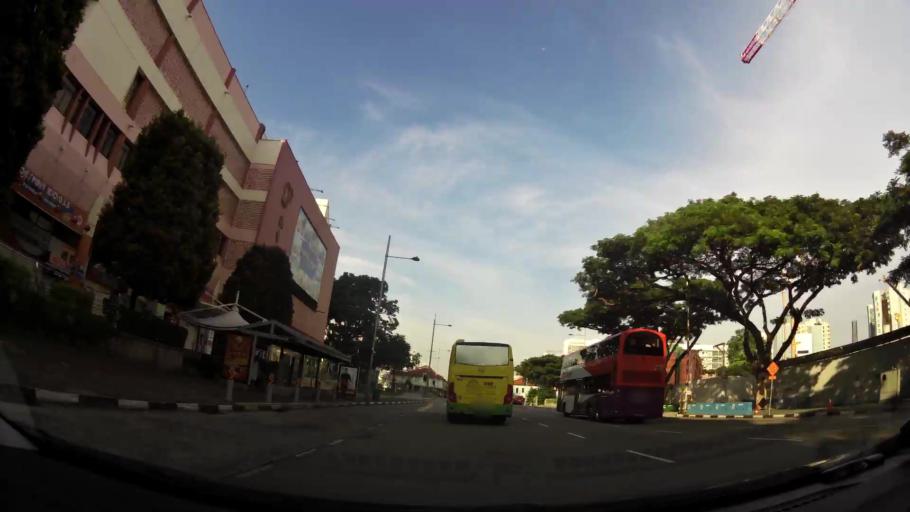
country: SG
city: Singapore
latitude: 1.3153
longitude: 103.8934
